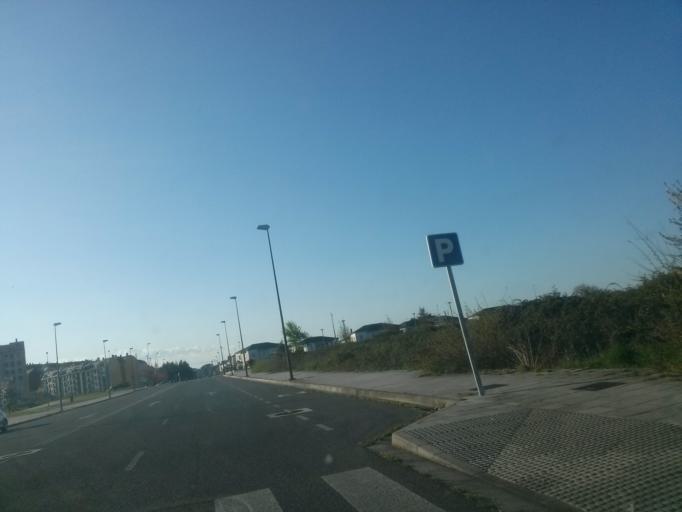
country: ES
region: Galicia
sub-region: Provincia de Lugo
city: Lugo
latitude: 43.0001
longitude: -7.5398
